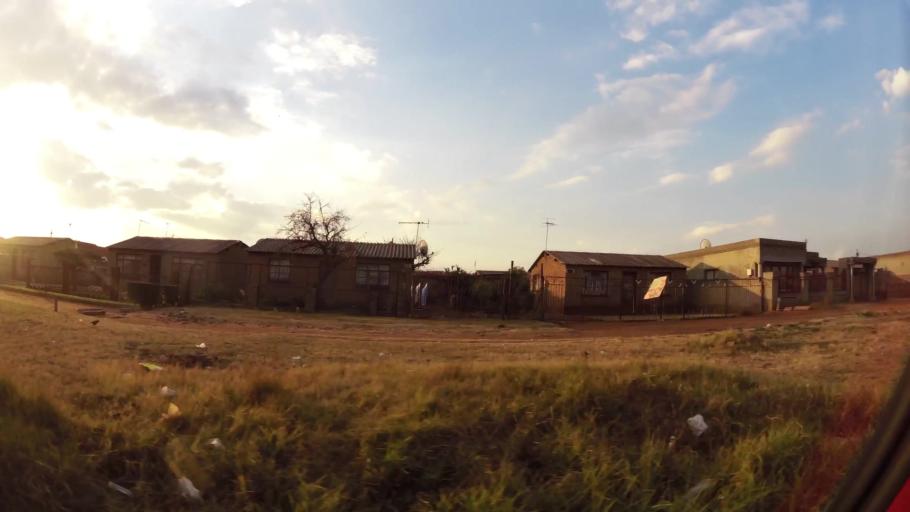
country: ZA
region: Gauteng
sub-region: City of Johannesburg Metropolitan Municipality
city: Orange Farm
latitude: -26.5936
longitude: 27.8311
